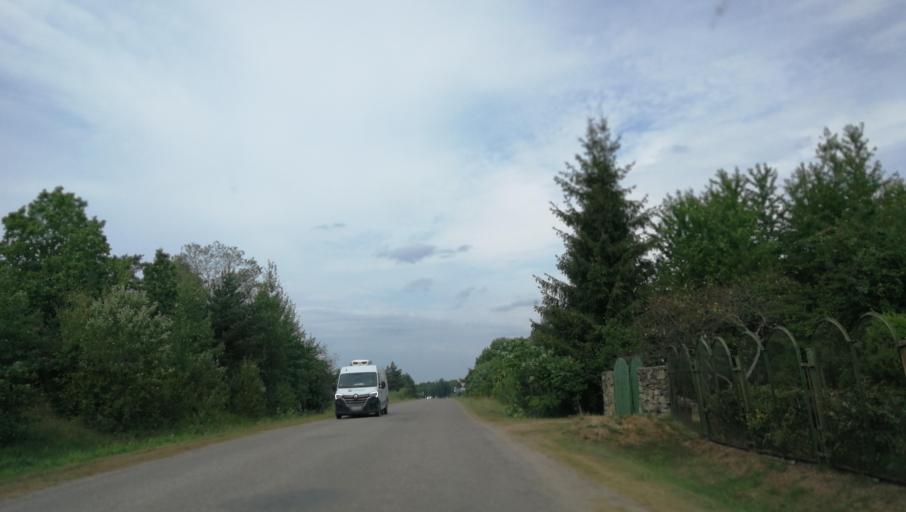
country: LV
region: Alsunga
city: Alsunga
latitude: 56.9775
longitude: 21.5552
